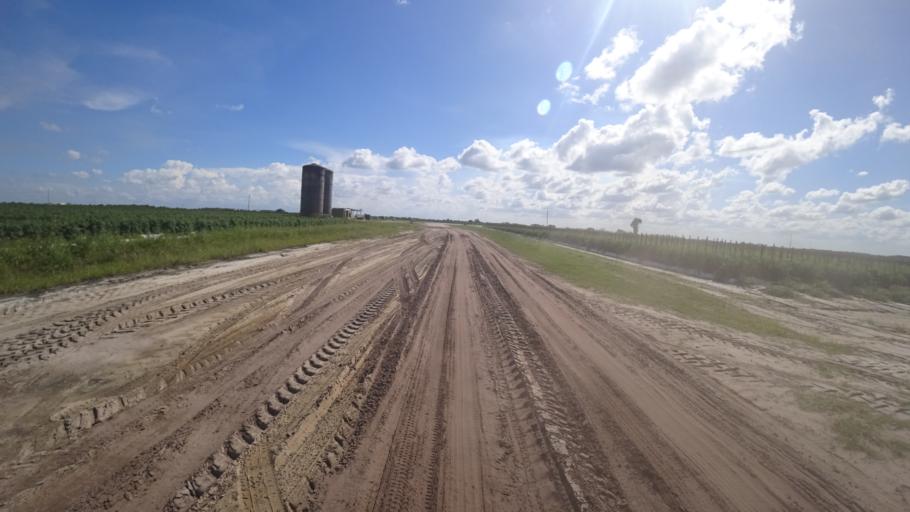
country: US
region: Florida
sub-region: DeSoto County
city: Arcadia
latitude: 27.3261
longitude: -82.0970
